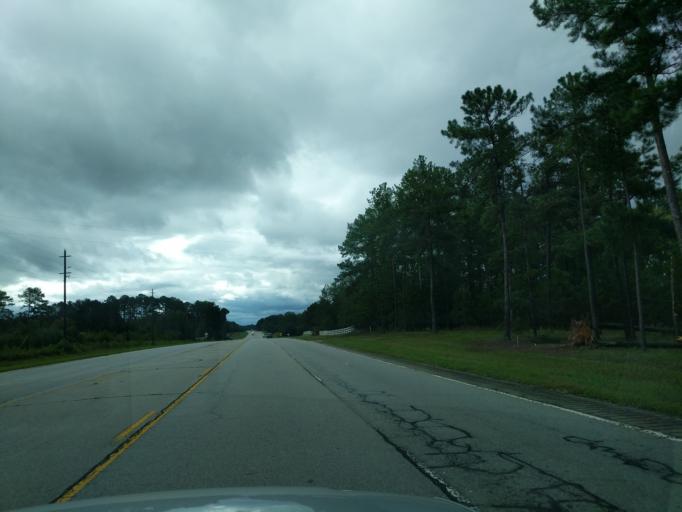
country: US
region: Georgia
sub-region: Wilkes County
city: Washington
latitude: 33.7137
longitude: -82.7022
